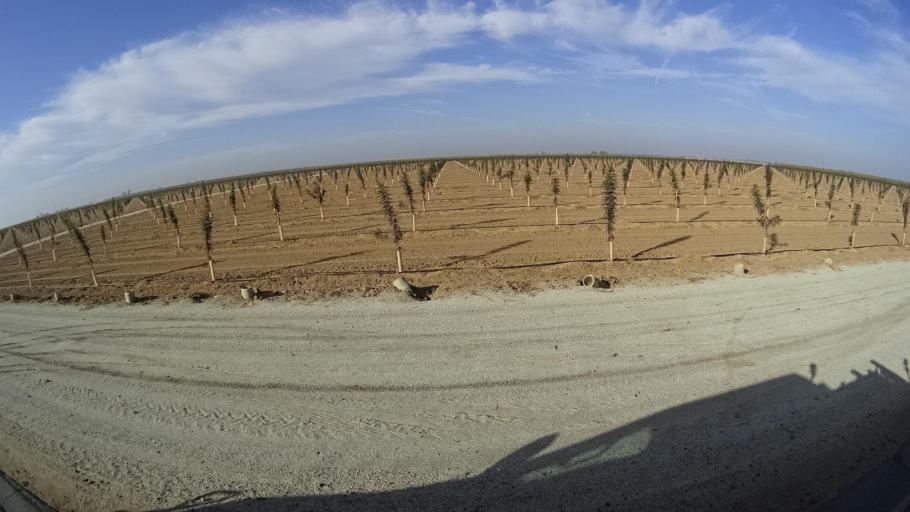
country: US
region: California
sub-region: Kern County
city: McFarland
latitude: 35.6570
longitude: -119.2046
